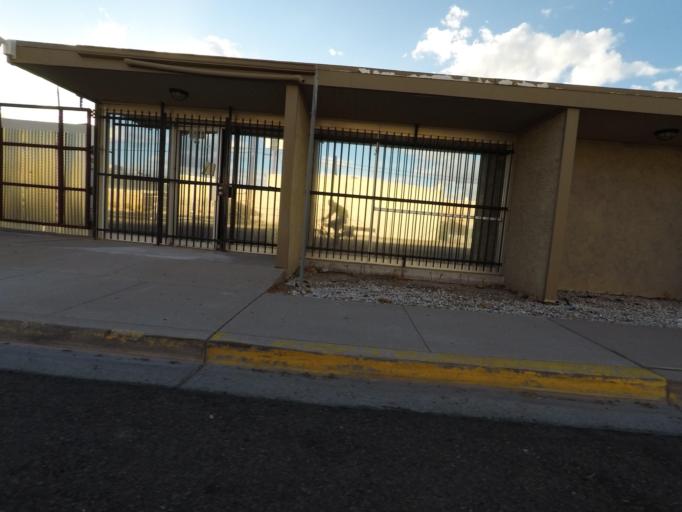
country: US
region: Arizona
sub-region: Maricopa County
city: Glendale
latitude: 33.4971
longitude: -112.1430
